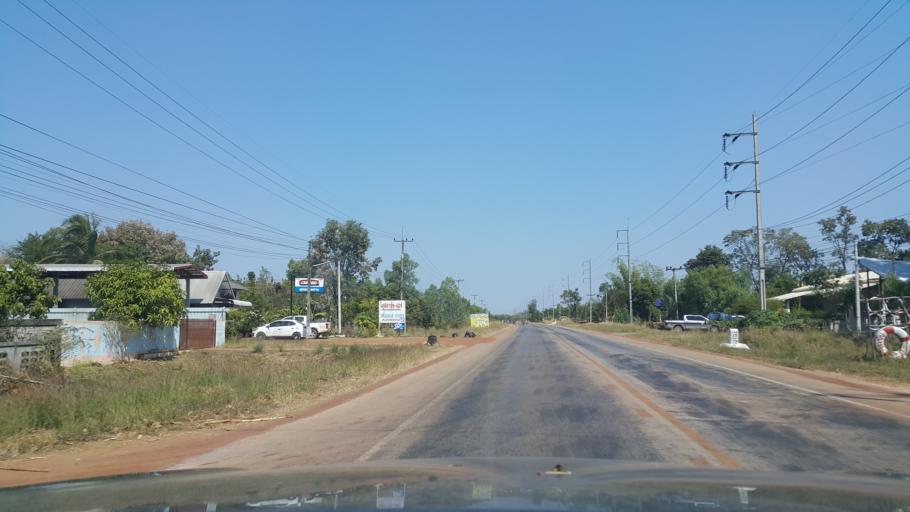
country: TH
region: Changwat Udon Thani
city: Thung Fon
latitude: 17.4905
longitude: 103.1983
